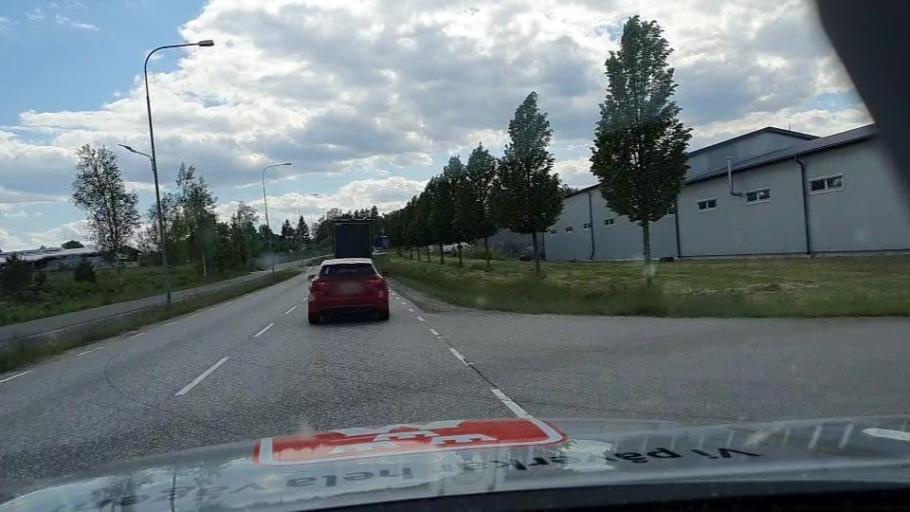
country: SE
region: Kronoberg
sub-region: Ljungby Kommun
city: Ljungby
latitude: 56.8454
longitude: 13.9206
